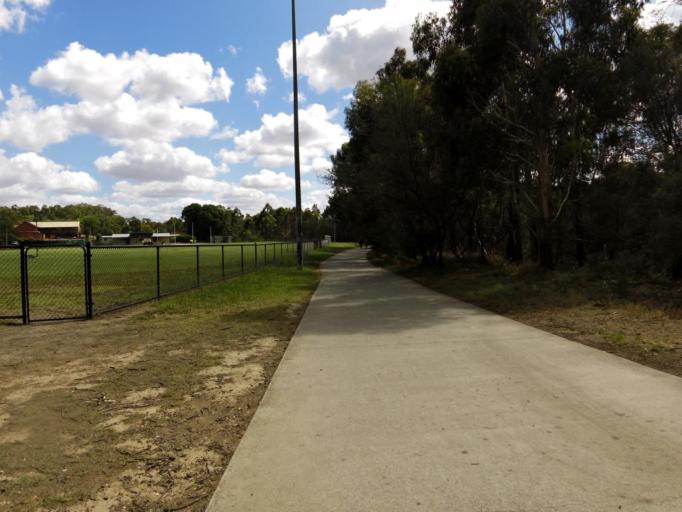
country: AU
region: Victoria
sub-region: Nillumbik
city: Eltham
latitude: -37.7213
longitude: 145.1421
